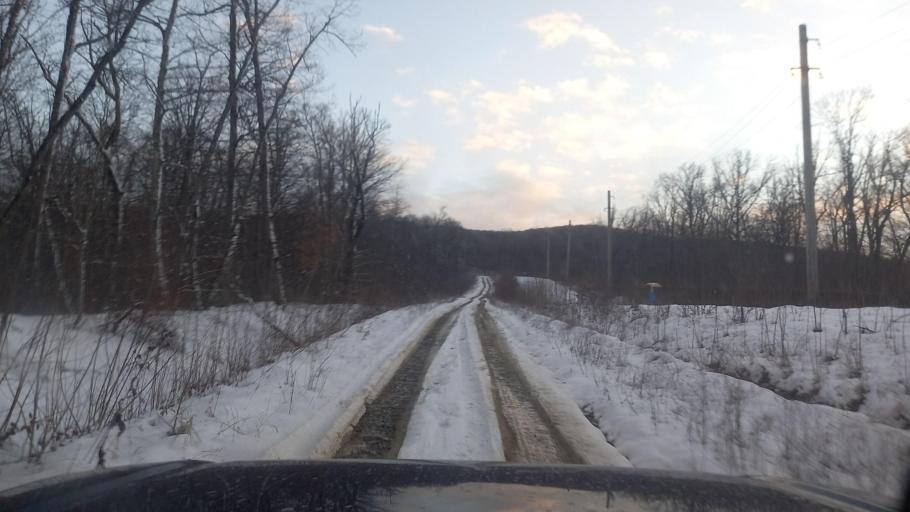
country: RU
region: Krasnodarskiy
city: Smolenskaya
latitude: 44.6731
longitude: 38.7965
